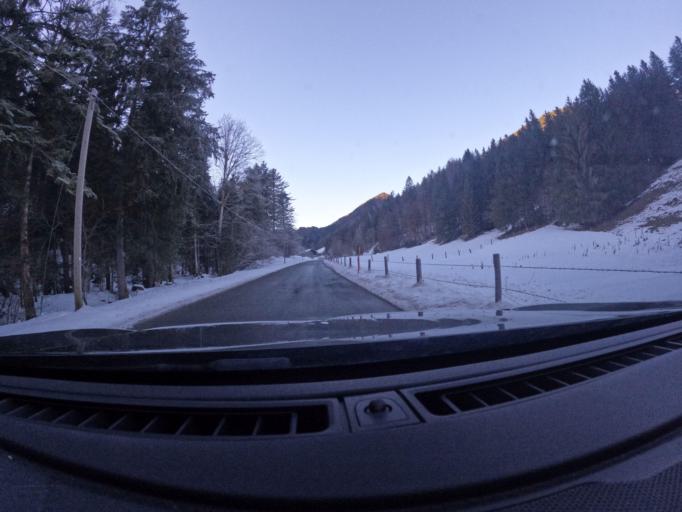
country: DE
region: Bavaria
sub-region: Upper Bavaria
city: Ruhpolding
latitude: 47.7601
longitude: 12.6166
